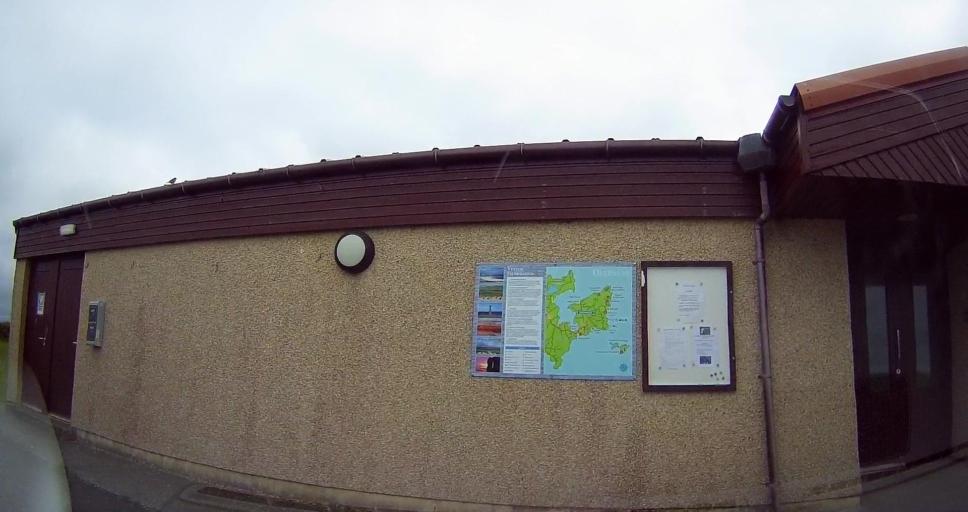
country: GB
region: Scotland
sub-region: Orkney Islands
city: Kirkwall
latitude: 58.9366
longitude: -2.7476
